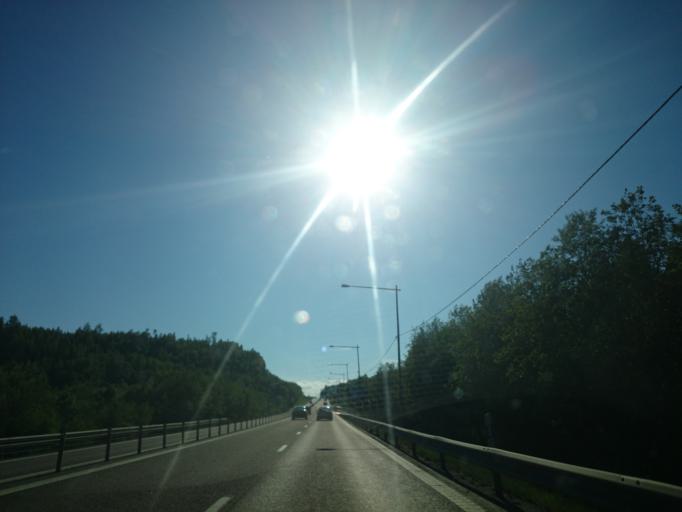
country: SE
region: Vaesternorrland
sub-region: Timra Kommun
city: Bergeforsen
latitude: 62.5177
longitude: 17.4206
